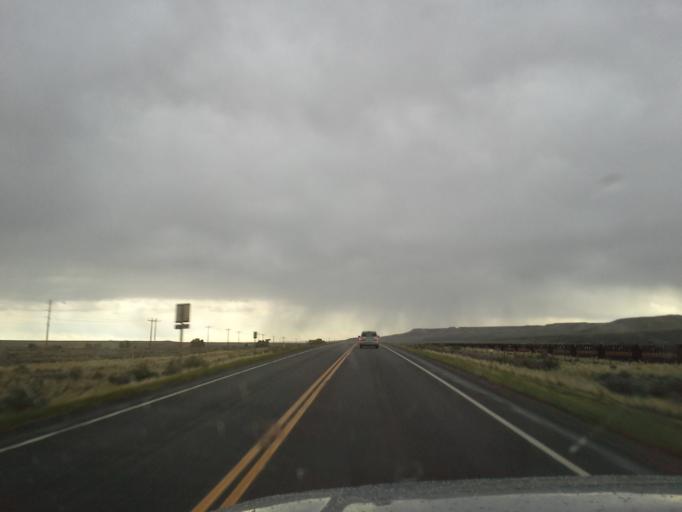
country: US
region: Wyoming
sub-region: Park County
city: Powell
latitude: 45.0530
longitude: -108.6553
